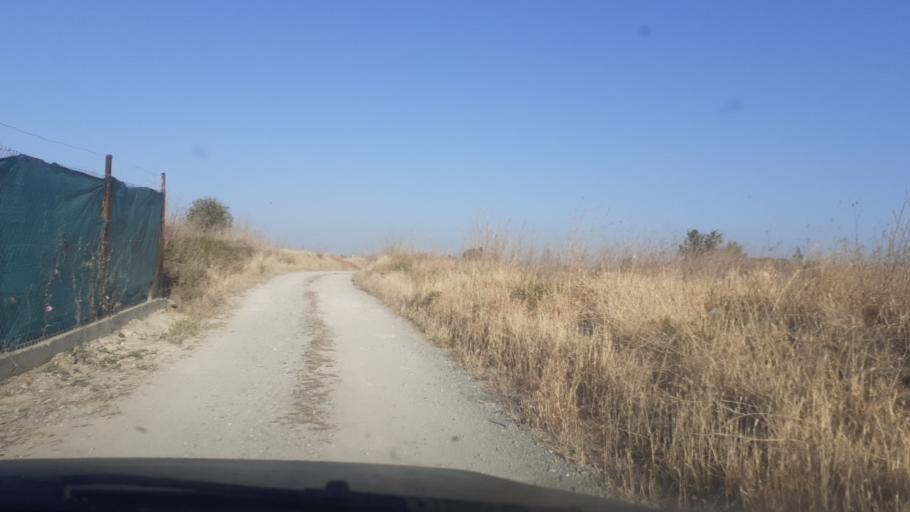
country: CY
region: Larnaka
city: Kolossi
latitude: 34.6677
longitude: 32.9420
